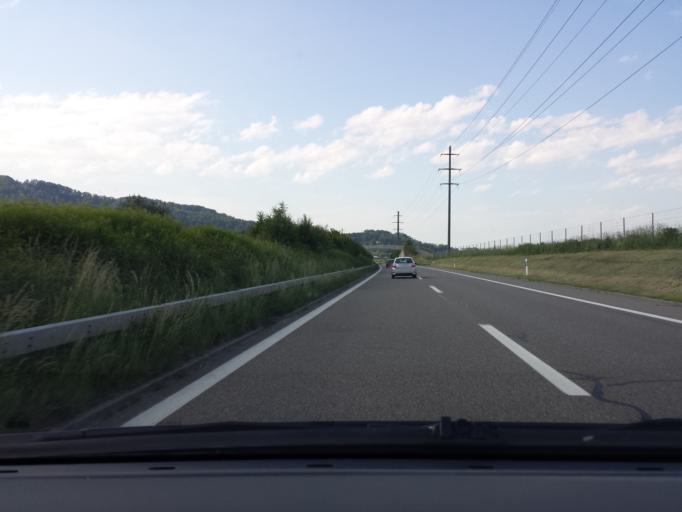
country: AT
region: Vorarlberg
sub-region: Politischer Bezirk Dornbirn
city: Lustenau
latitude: 47.4232
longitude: 9.6466
